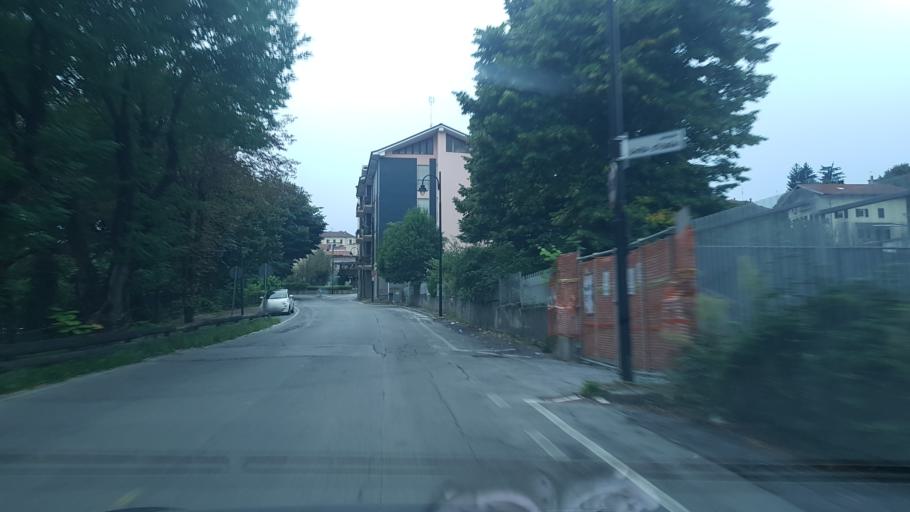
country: IT
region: Piedmont
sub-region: Provincia di Cuneo
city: Mondovi
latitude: 44.3880
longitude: 7.8187
